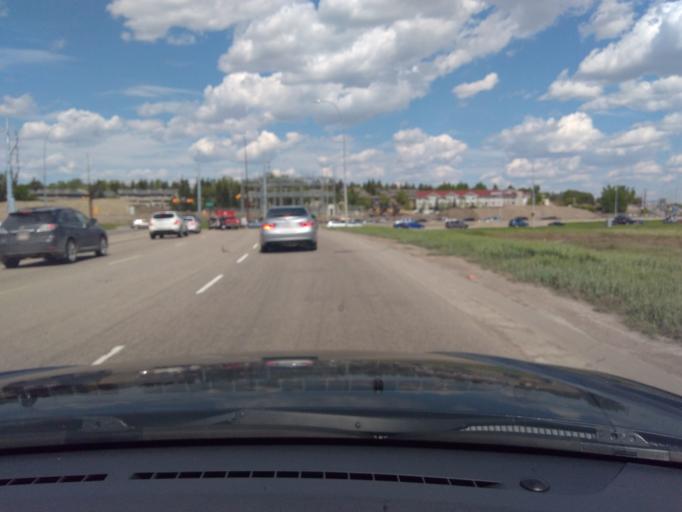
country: CA
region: Alberta
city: Calgary
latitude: 51.0090
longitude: -114.1642
